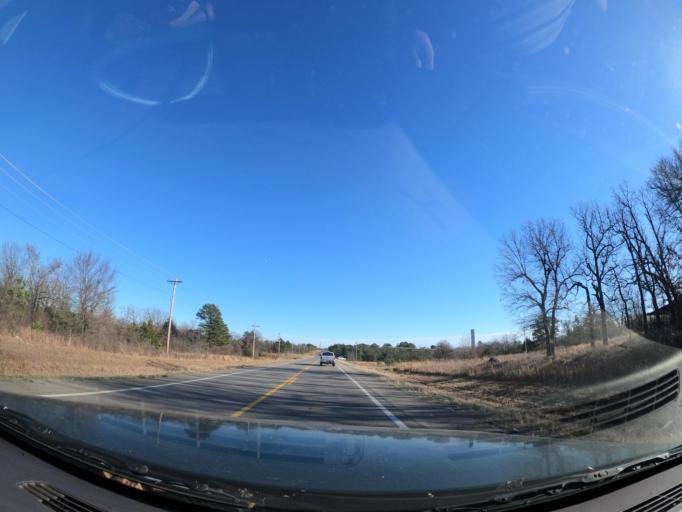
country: US
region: Oklahoma
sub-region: Pittsburg County
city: Longtown
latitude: 35.2340
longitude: -95.4613
